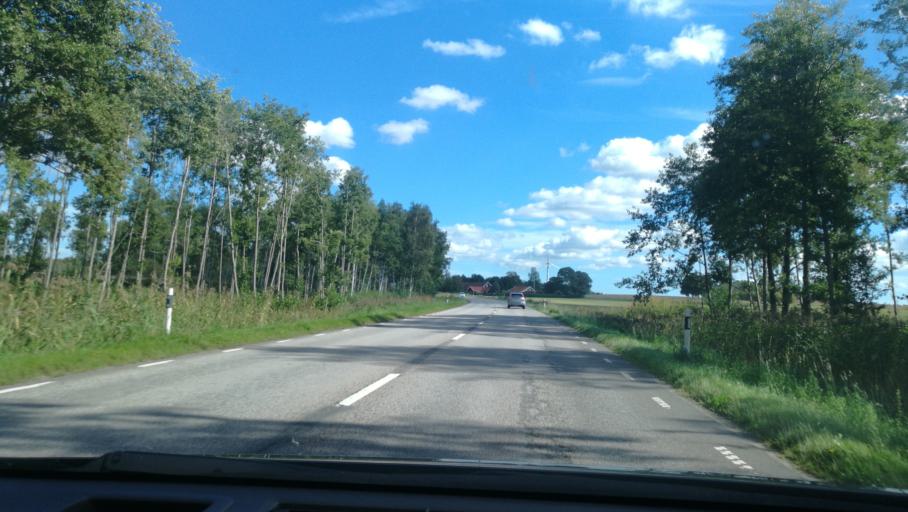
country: SE
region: Vaestra Goetaland
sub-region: Gotene Kommun
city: Kallby
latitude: 58.4910
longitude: 13.2834
